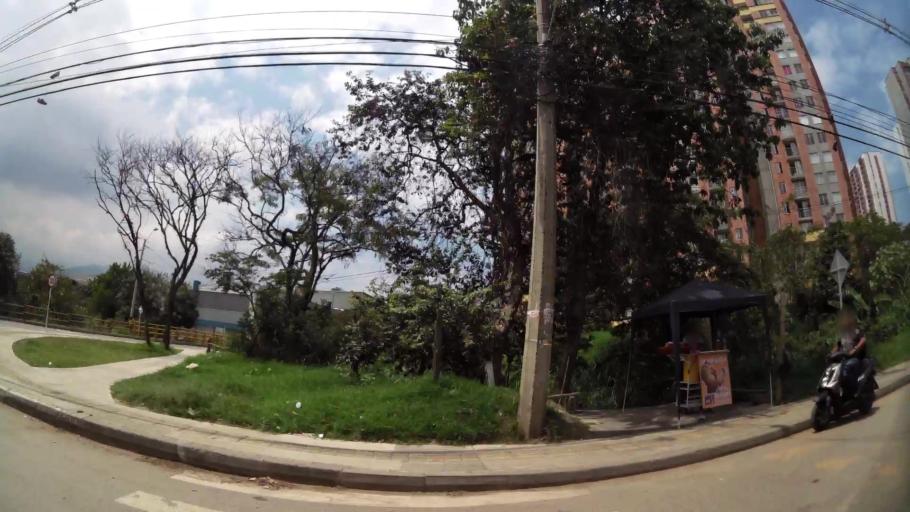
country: CO
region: Antioquia
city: Itagui
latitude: 6.1905
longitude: -75.6021
